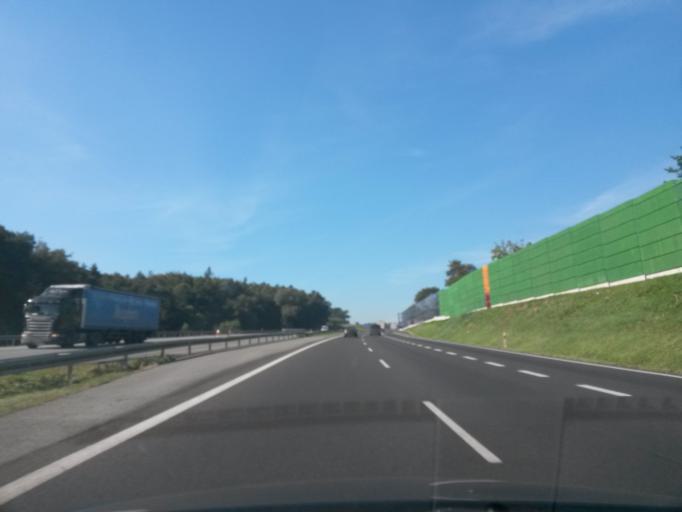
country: PL
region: Lesser Poland Voivodeship
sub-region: Powiat krakowski
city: Mnikow
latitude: 50.0770
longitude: 19.7157
